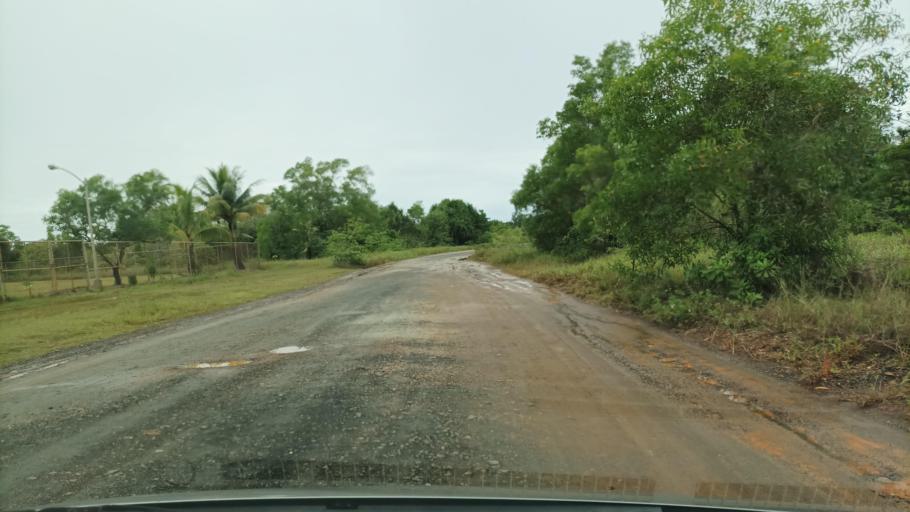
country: FM
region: Yap
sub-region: Weloy Municipality
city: Colonia
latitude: 9.5454
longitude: 138.1654
